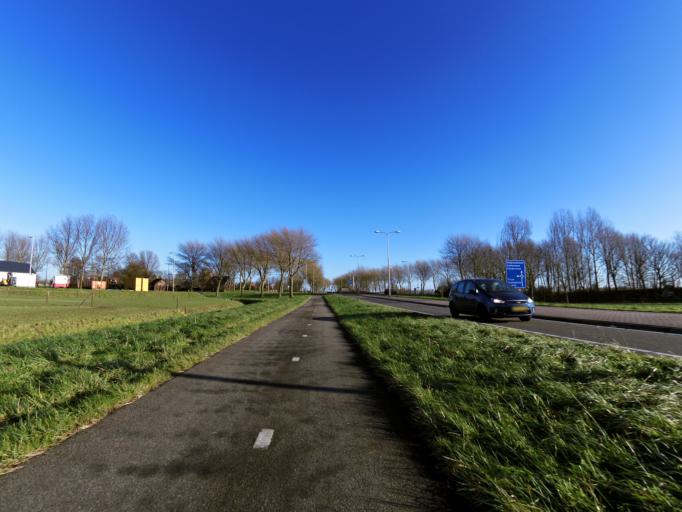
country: NL
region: South Holland
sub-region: Gemeente Hellevoetsluis
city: Nieuw-Helvoet
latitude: 51.8728
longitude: 4.0892
